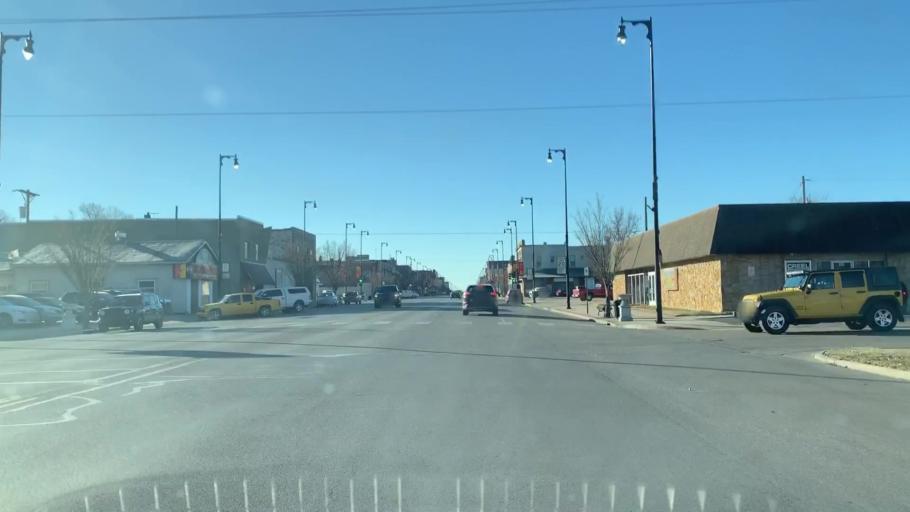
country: US
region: Kansas
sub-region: Crawford County
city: Pittsburg
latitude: 37.4181
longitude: -94.7050
